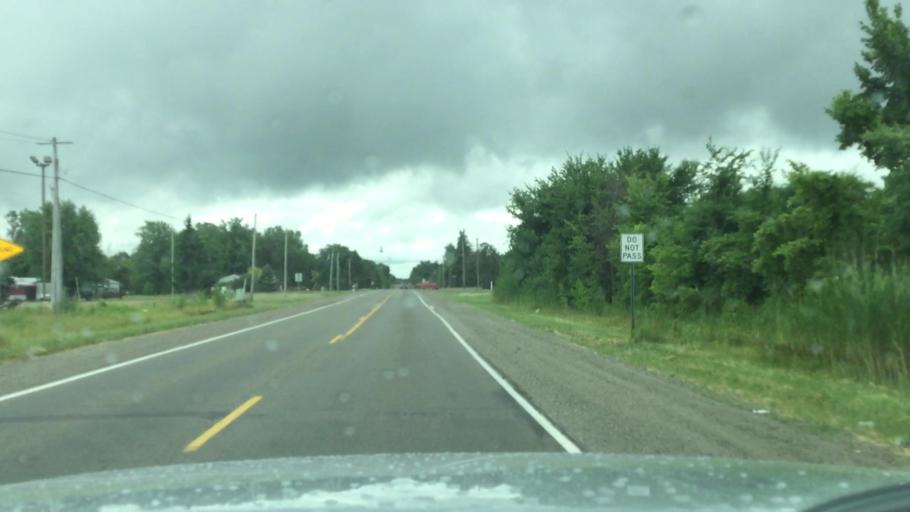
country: US
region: Michigan
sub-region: Genesee County
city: Flushing
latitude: 43.0695
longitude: -83.7732
